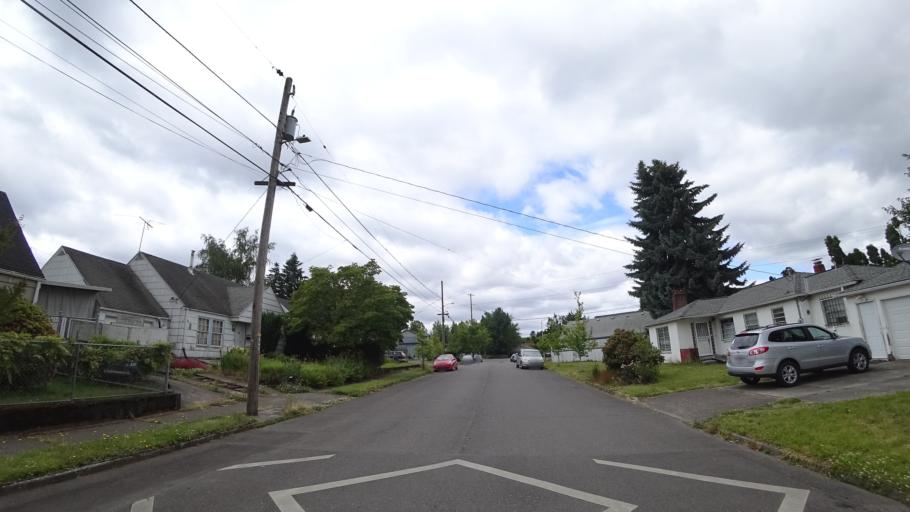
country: US
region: Oregon
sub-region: Multnomah County
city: Lents
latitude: 45.5600
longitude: -122.5956
